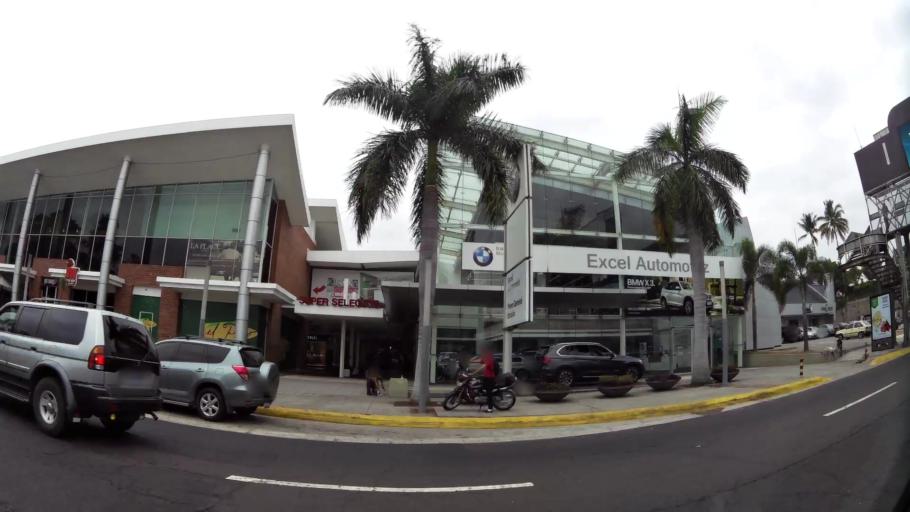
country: SV
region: La Libertad
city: Antiguo Cuscatlan
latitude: 13.7023
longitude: -89.2355
